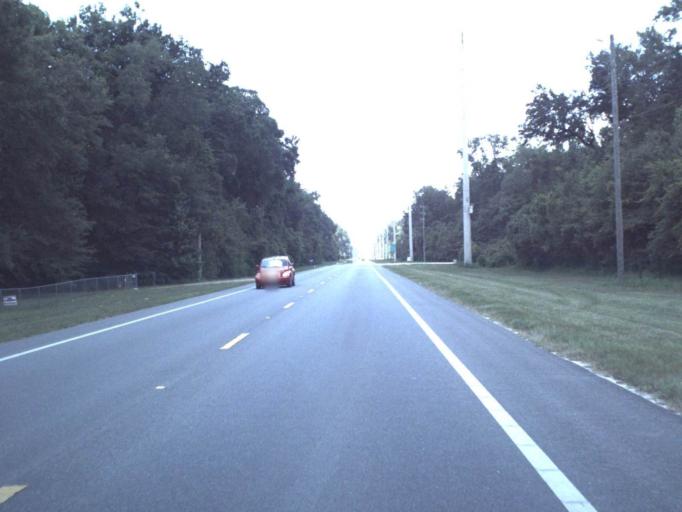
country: US
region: Florida
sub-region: Levy County
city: Manatee Road
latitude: 29.6316
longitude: -82.9833
